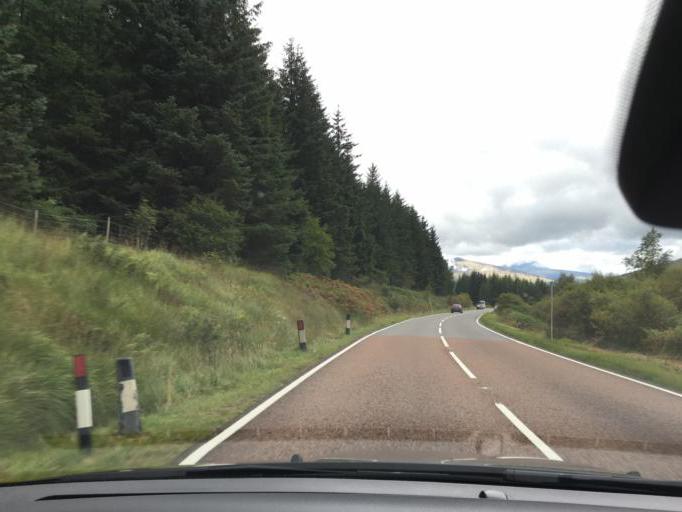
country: GB
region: Scotland
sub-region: Argyll and Bute
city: Garelochhead
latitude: 56.4789
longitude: -4.7330
